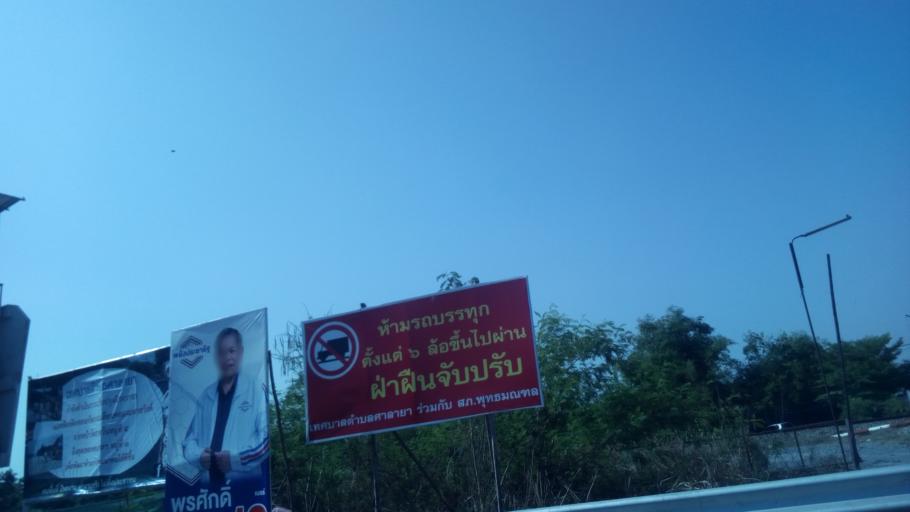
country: TH
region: Nakhon Pathom
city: Salaya
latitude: 13.8033
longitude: 100.3038
